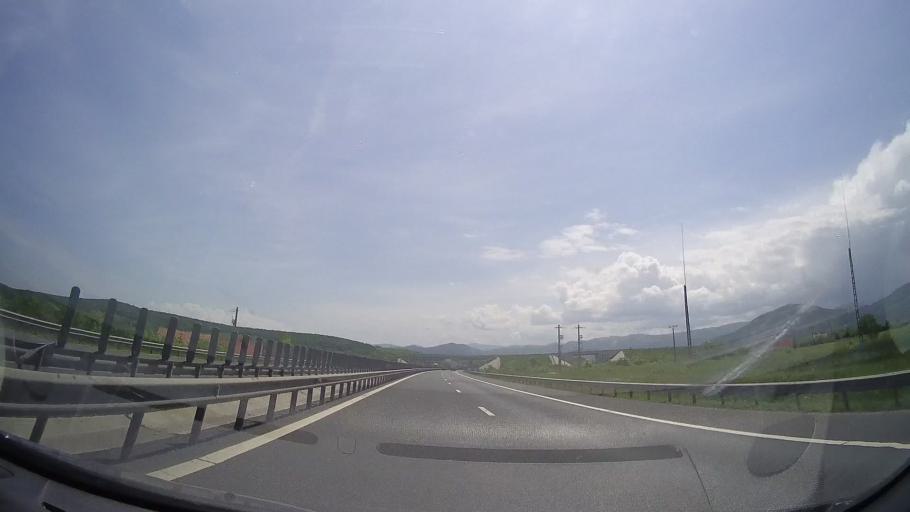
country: RO
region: Sibiu
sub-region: Comuna Orlat
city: Orlat
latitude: 45.7901
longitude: 23.9431
